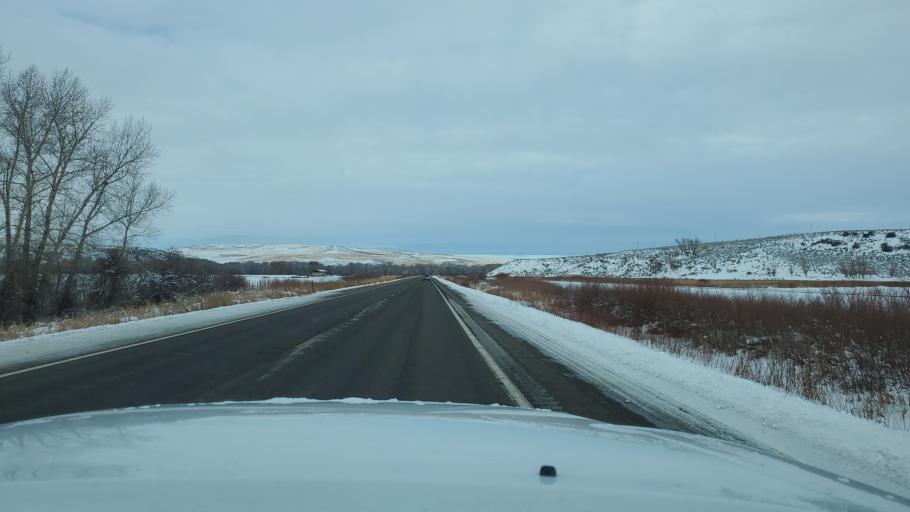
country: US
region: Colorado
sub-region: Routt County
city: Hayden
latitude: 40.4934
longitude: -107.3563
